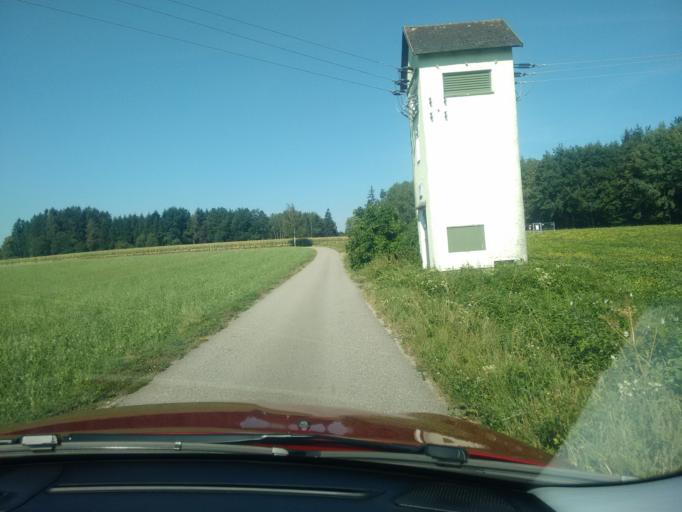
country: AT
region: Upper Austria
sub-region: Wels-Land
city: Sattledt
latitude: 48.0973
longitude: 14.0501
